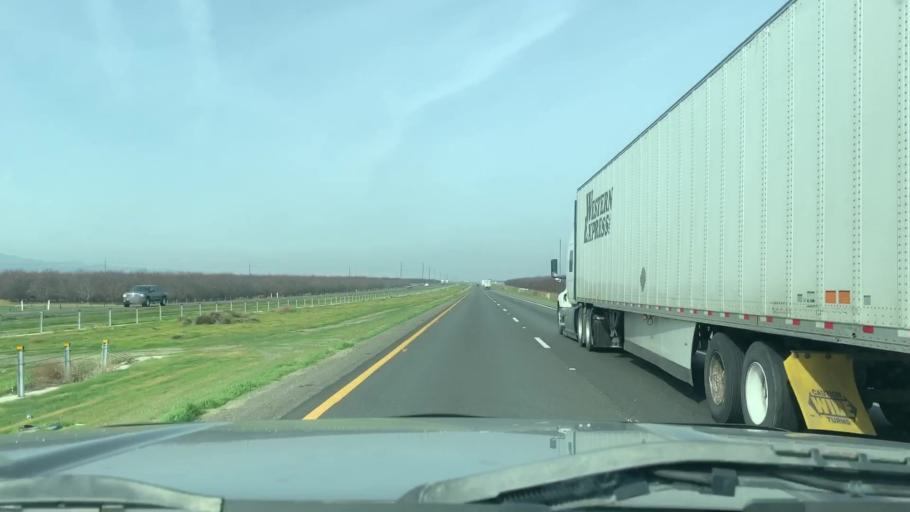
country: US
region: California
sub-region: Fresno County
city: Huron
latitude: 36.2250
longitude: -120.2253
